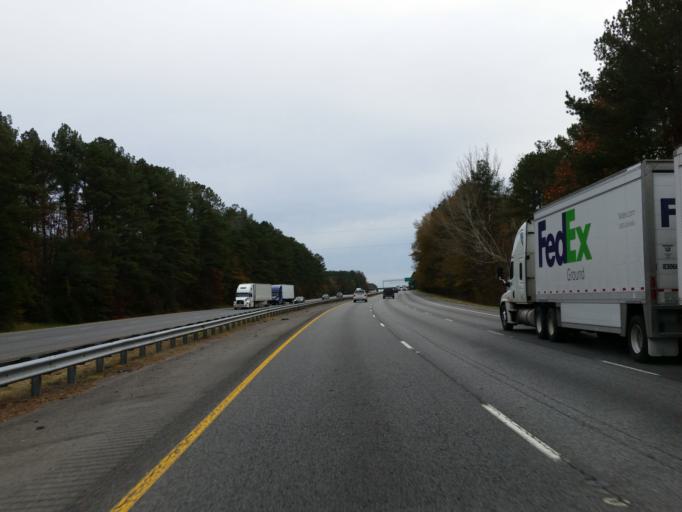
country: US
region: Georgia
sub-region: Monroe County
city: Forsyth
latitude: 33.1210
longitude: -84.0045
